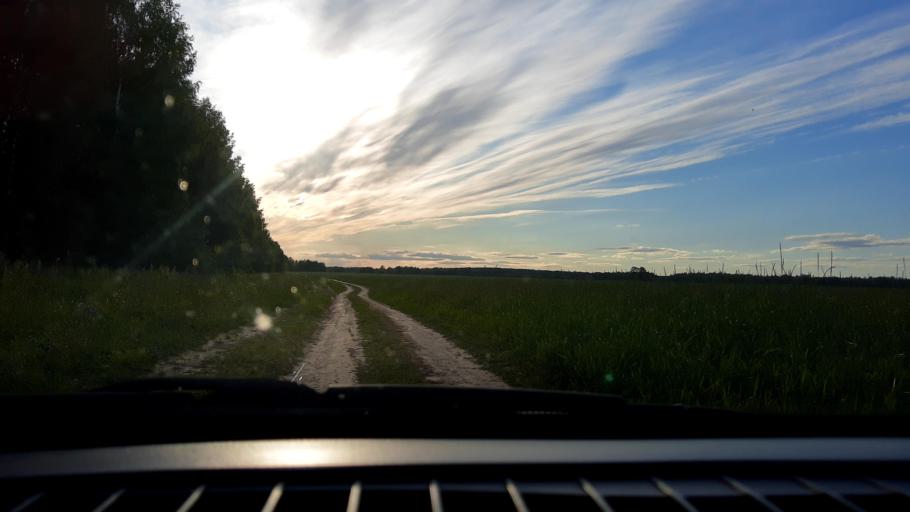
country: RU
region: Nizjnij Novgorod
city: Kstovo
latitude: 56.2617
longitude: 44.3228
